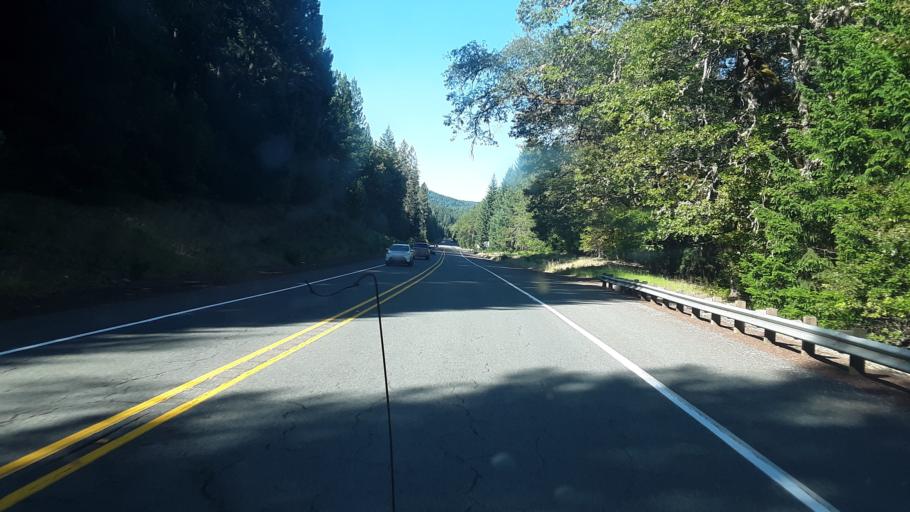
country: US
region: Oregon
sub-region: Jackson County
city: Shady Cove
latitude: 42.6857
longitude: -122.6101
